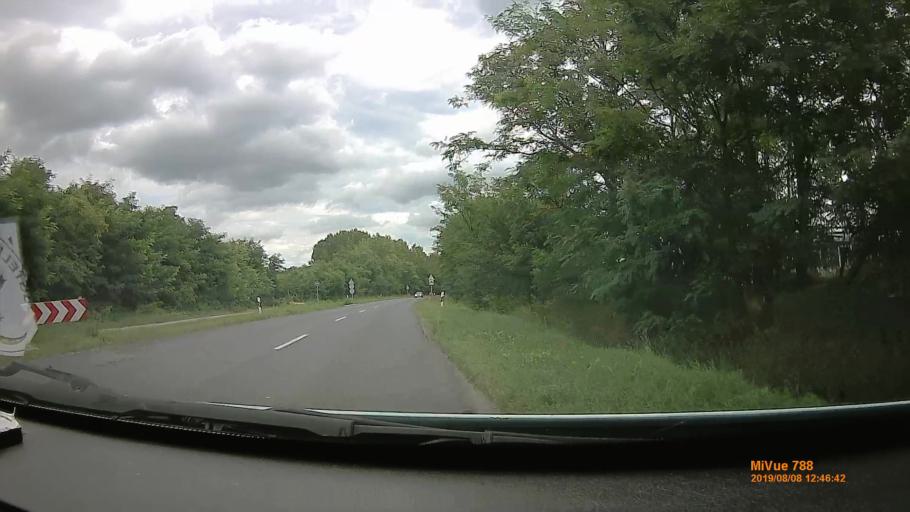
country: HU
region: Szabolcs-Szatmar-Bereg
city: Hodasz
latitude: 47.8988
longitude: 22.2236
